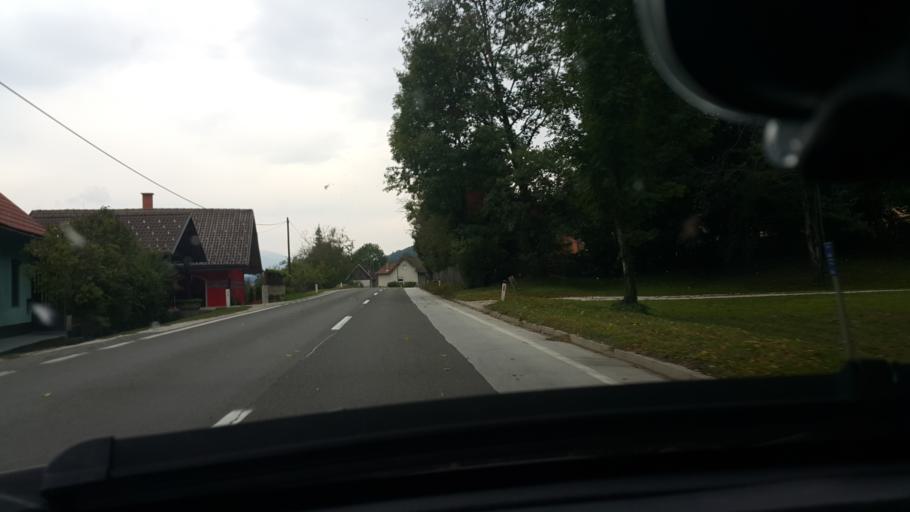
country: SI
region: Ruse
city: Bistrica ob Dravi
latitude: 46.5599
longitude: 15.5297
